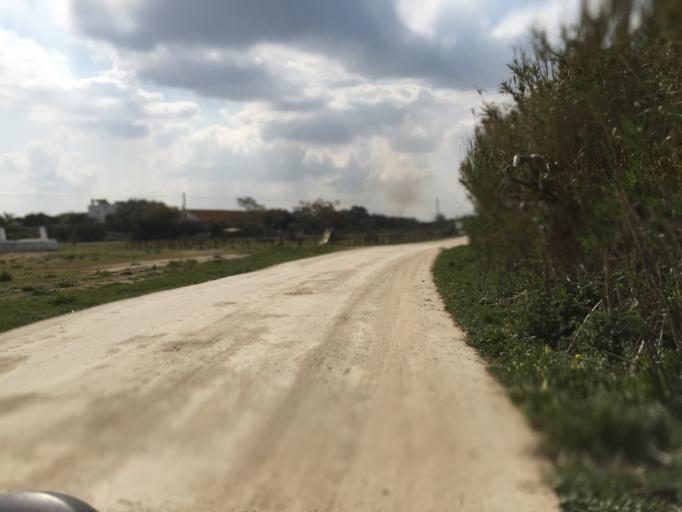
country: ES
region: Andalusia
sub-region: Provincia de Cadiz
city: Benalup-Casas Viejas
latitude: 36.3238
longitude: -5.8841
